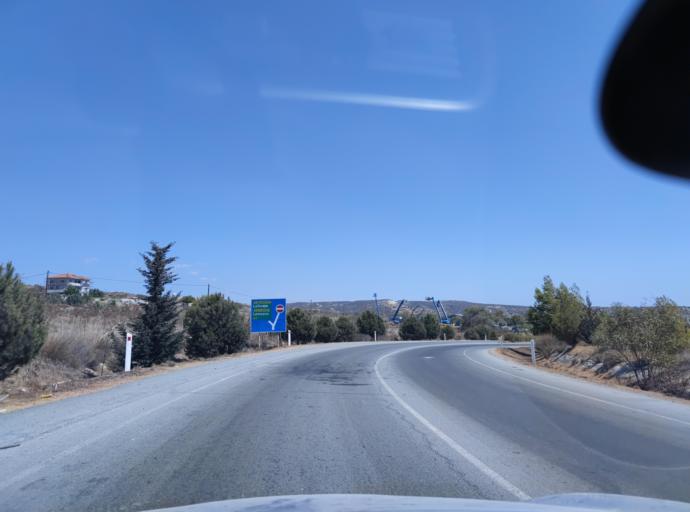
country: CY
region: Larnaka
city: Kofinou
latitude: 34.7570
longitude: 33.3165
